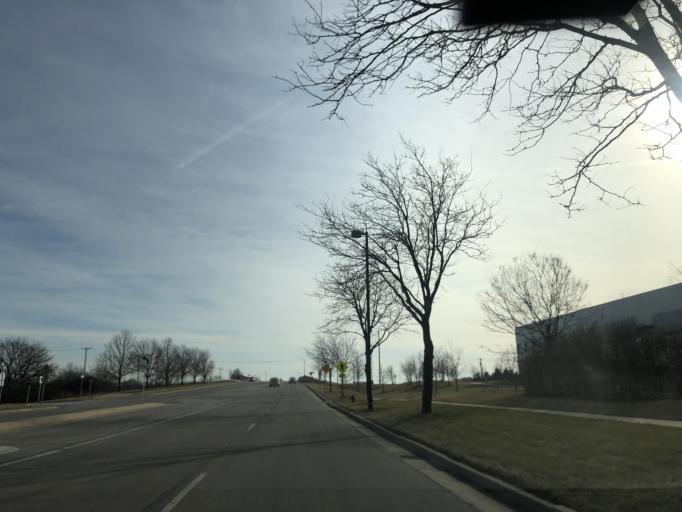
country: US
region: Illinois
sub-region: Will County
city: Bolingbrook
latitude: 41.7102
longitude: -88.0264
